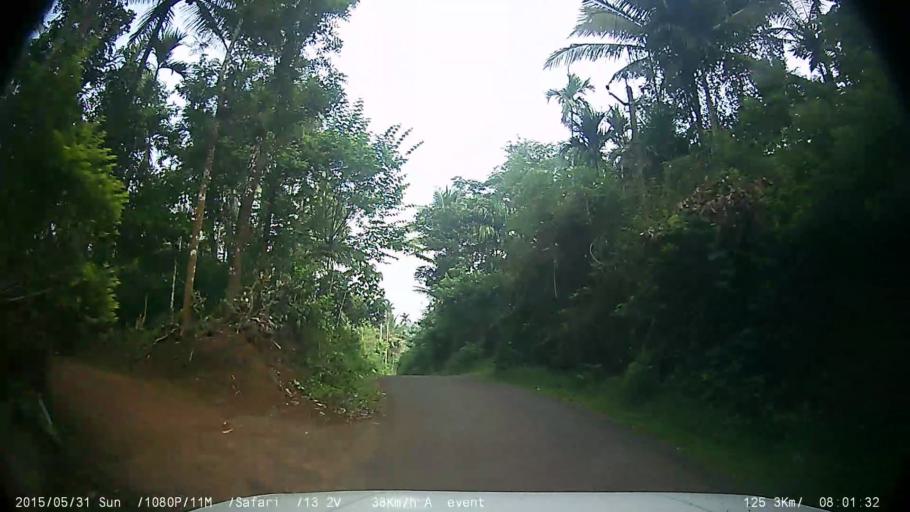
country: IN
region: Kerala
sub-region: Wayanad
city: Kalpetta
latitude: 11.6330
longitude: 76.0463
